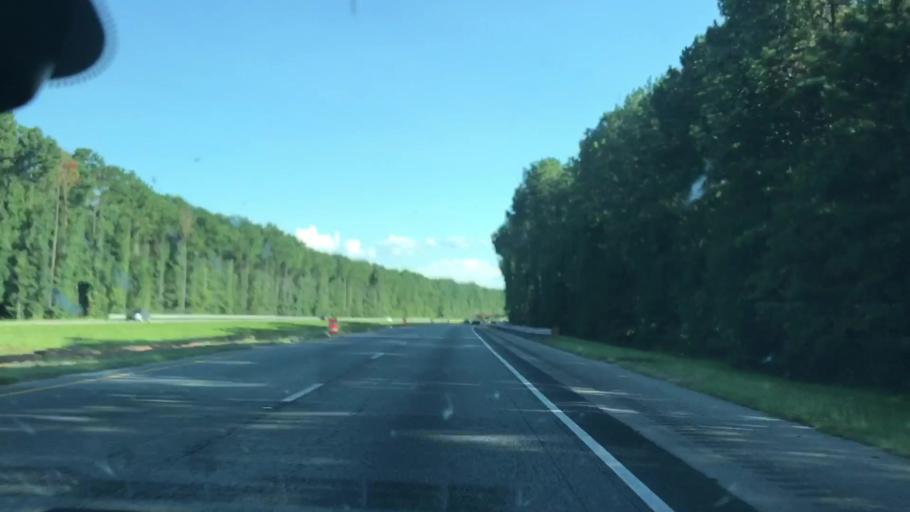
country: US
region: Georgia
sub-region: Harris County
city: Hamilton
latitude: 32.7627
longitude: -85.0180
